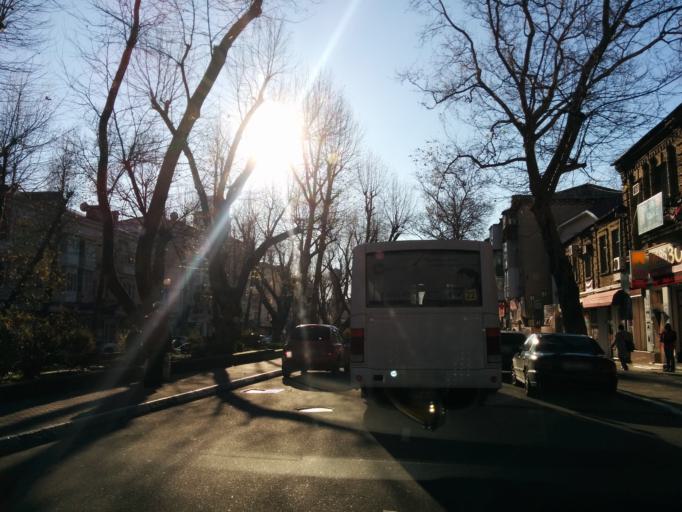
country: RU
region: Krasnodarskiy
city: Tuapse
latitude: 44.0994
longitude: 39.0786
